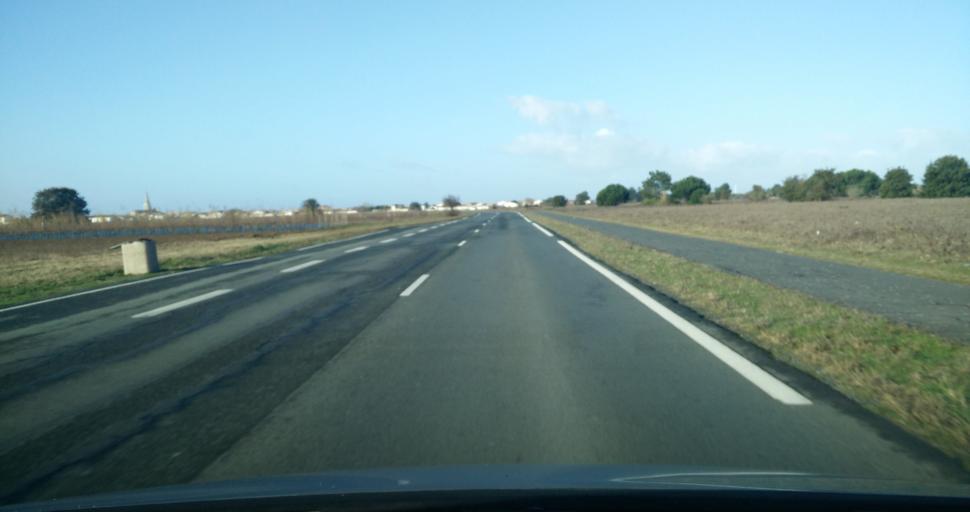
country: FR
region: Poitou-Charentes
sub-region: Departement de la Charente-Maritime
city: Sainte-Marie-de-Re
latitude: 46.1536
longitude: -1.2988
